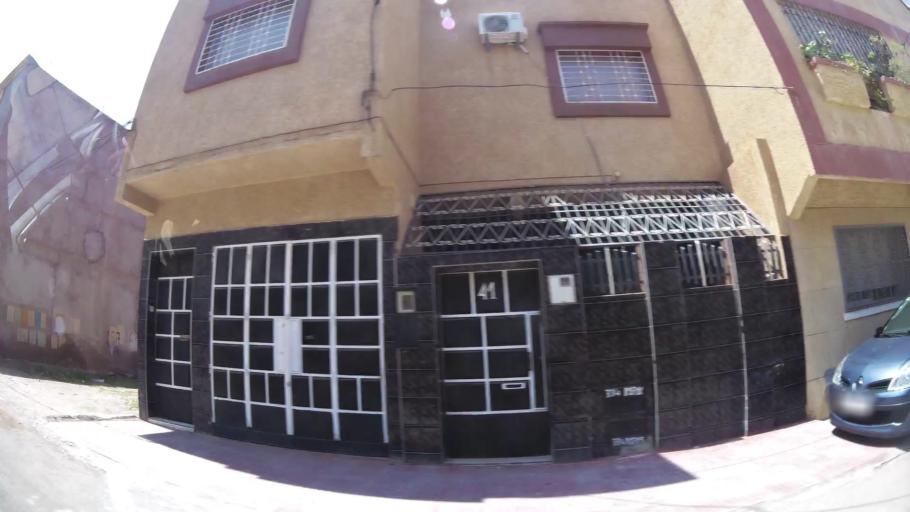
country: MA
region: Oriental
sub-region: Oujda-Angad
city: Oujda
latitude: 34.6827
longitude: -1.8909
